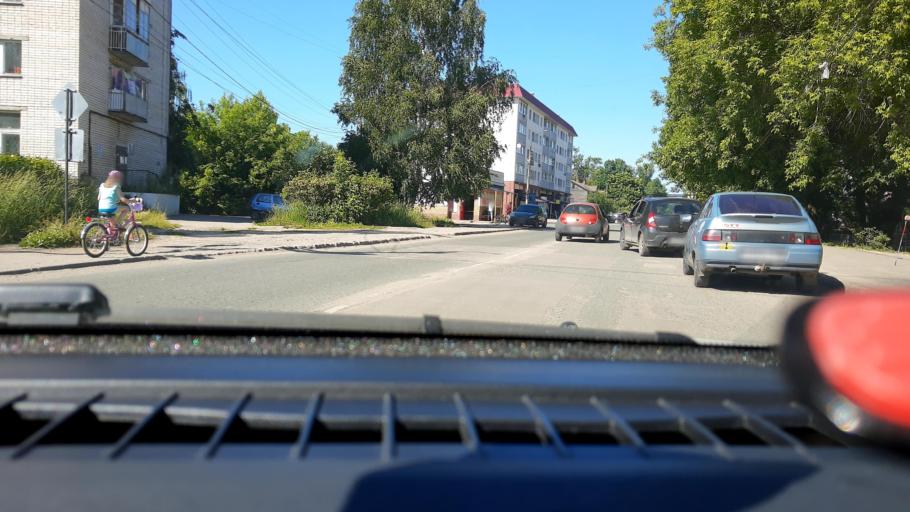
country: RU
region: Nizjnij Novgorod
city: Gidrotorf
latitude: 56.5211
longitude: 43.5486
